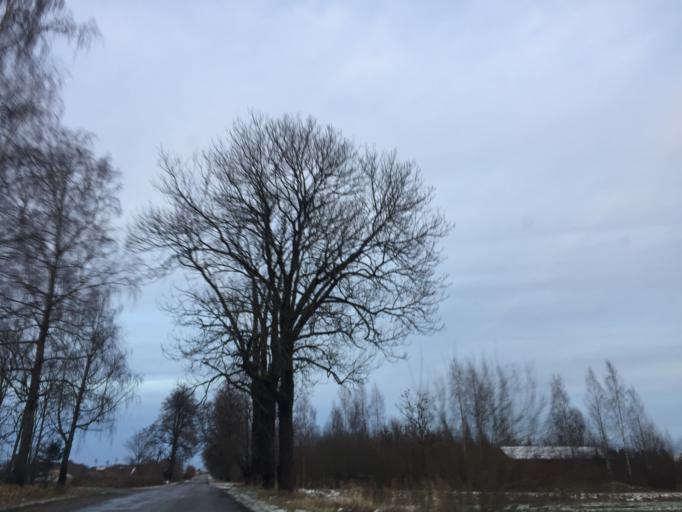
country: LV
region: Aloja
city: Aloja
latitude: 57.6034
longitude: 24.8636
